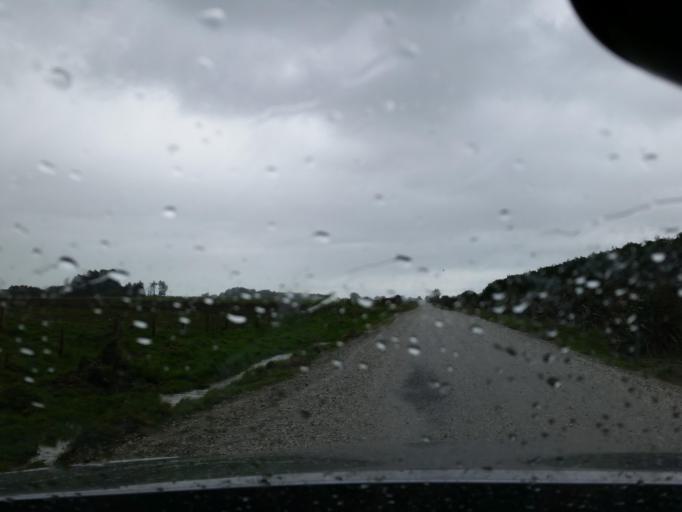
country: NZ
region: Southland
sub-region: Invercargill City
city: Invercargill
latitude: -46.4413
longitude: 168.5062
